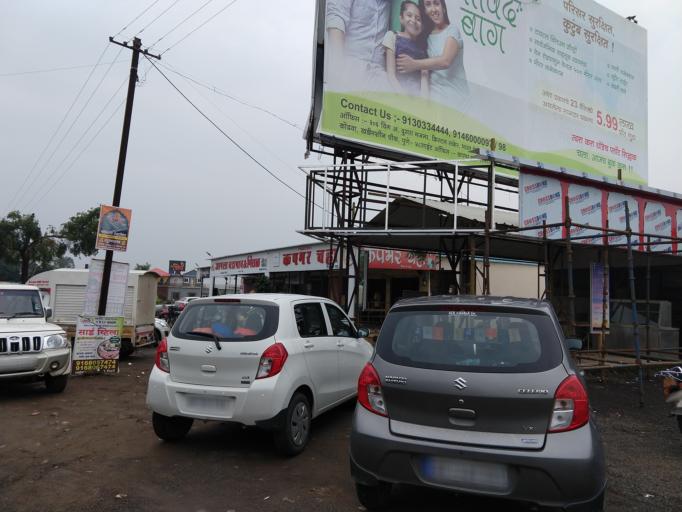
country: IN
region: Maharashtra
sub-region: Pune Division
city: Khed
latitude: 18.4024
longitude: 73.9118
